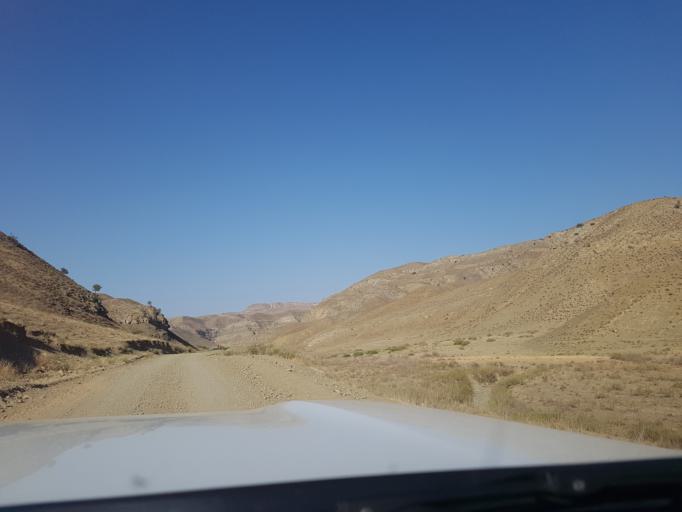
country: TM
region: Balkan
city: Magtymguly
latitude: 38.3010
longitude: 56.7644
